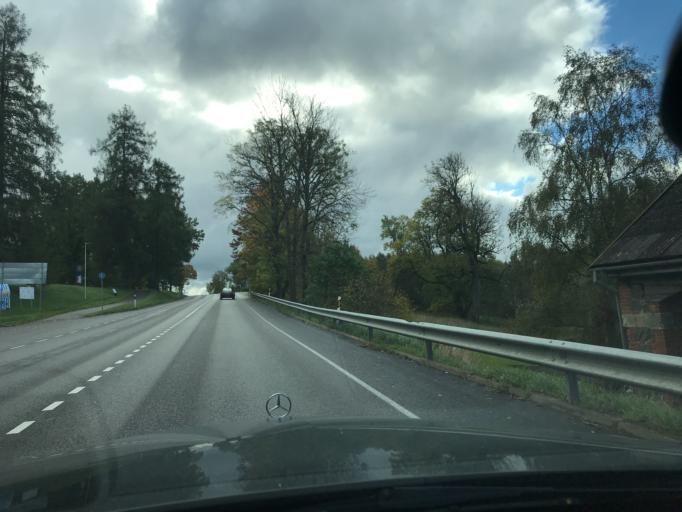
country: EE
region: Valgamaa
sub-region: Torva linn
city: Torva
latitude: 58.0162
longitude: 25.8786
